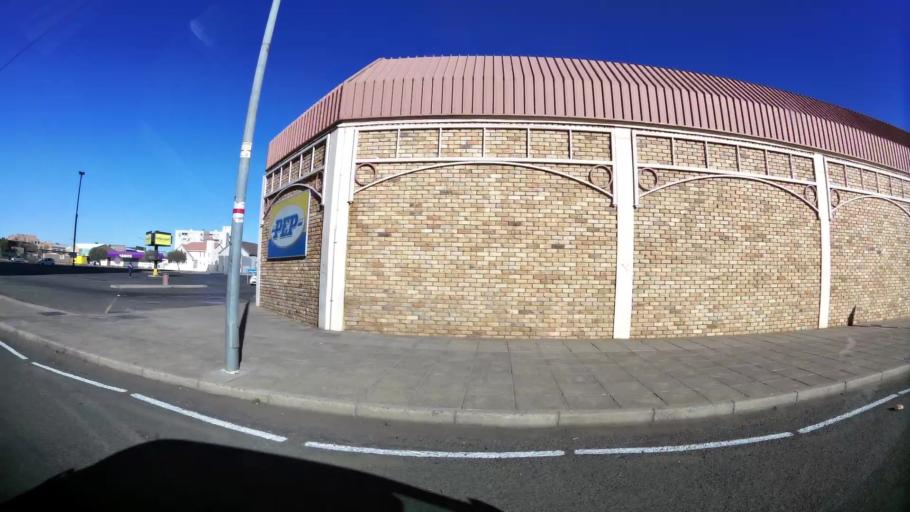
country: ZA
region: Northern Cape
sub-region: Frances Baard District Municipality
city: Kimberley
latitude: -28.7440
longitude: 24.7651
